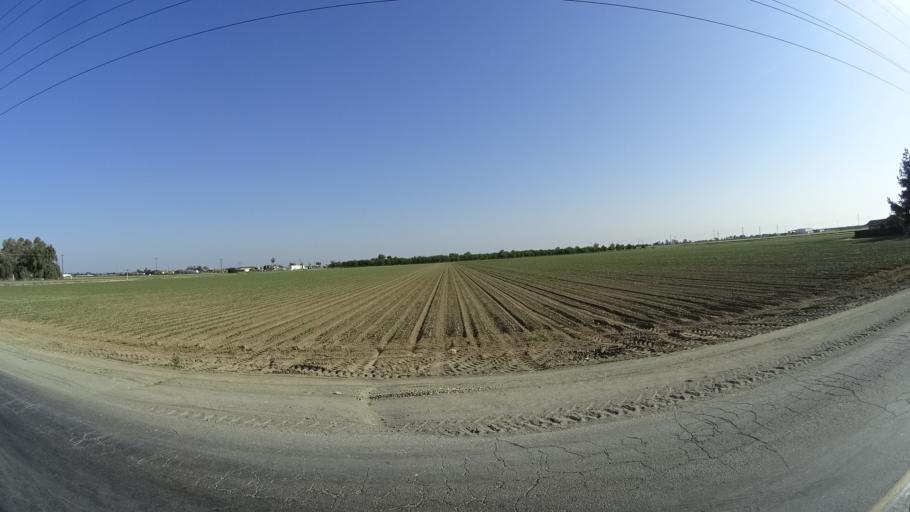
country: US
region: California
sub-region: Kings County
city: Home Garden
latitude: 36.3134
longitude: -119.5992
